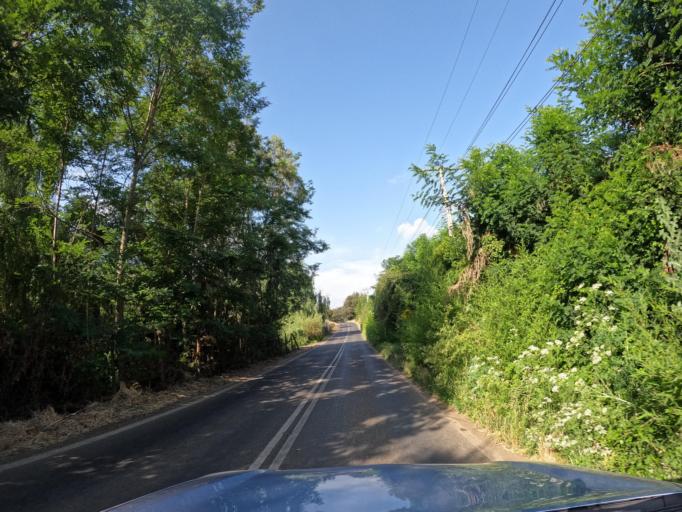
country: CL
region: Maule
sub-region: Provincia de Curico
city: Molina
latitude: -35.2716
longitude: -71.2489
